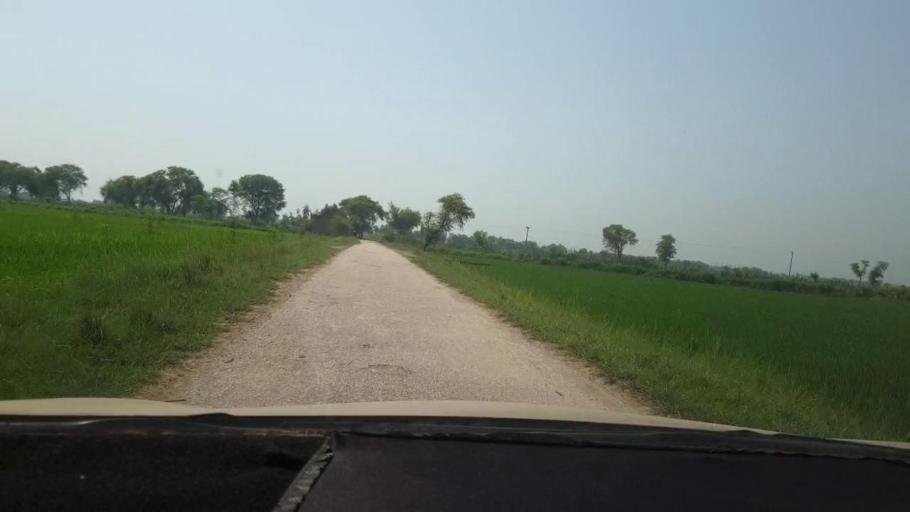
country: PK
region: Sindh
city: Miro Khan
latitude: 27.7095
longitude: 68.0387
